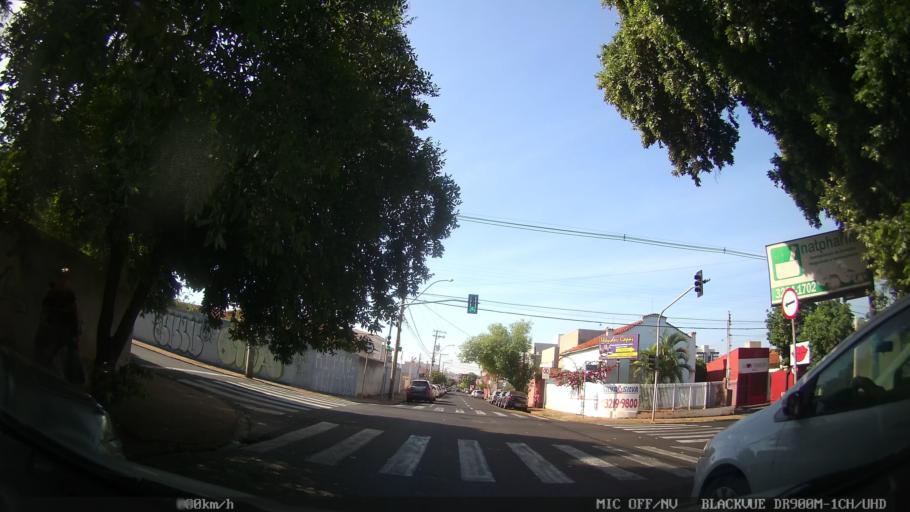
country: BR
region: Sao Paulo
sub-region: Sao Jose Do Rio Preto
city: Sao Jose do Rio Preto
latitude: -20.8032
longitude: -49.3855
